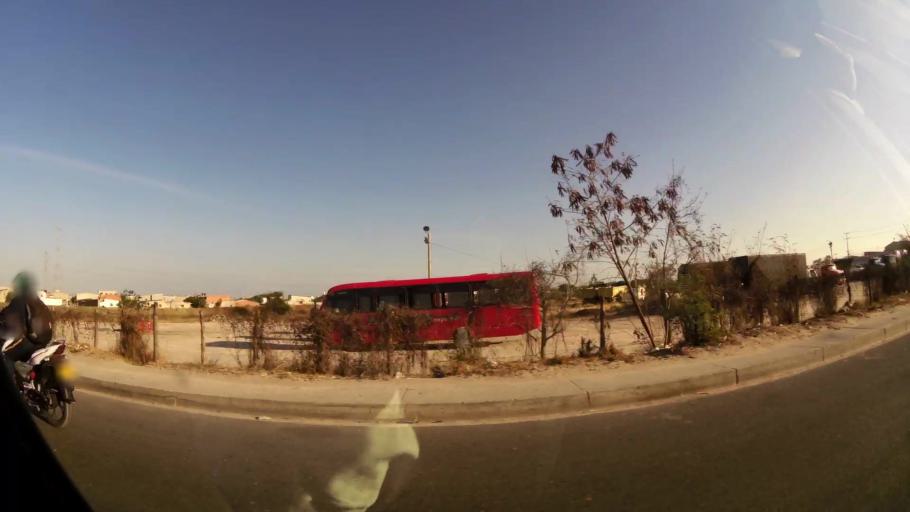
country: CO
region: Atlantico
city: Soledad
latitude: 10.9259
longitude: -74.7890
